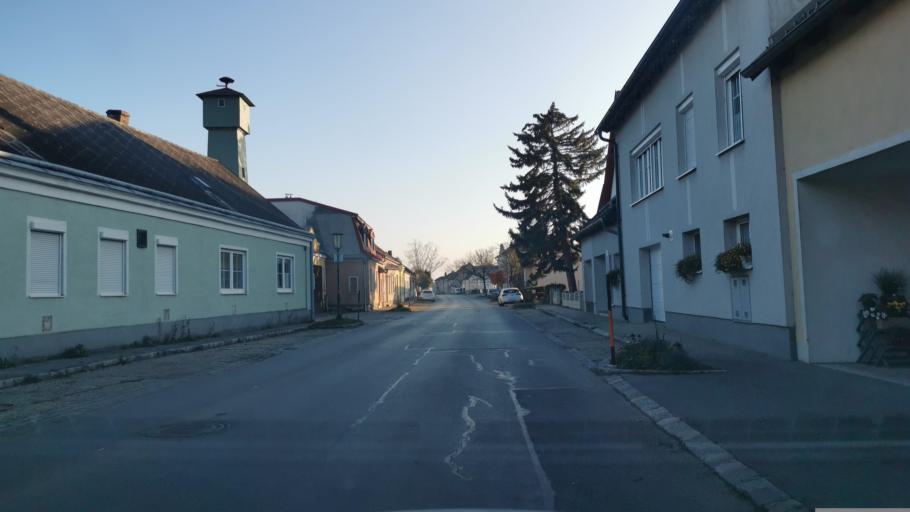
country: AT
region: Lower Austria
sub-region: Politischer Bezirk Korneuburg
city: Harmannsdorf
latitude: 48.3931
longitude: 16.3712
